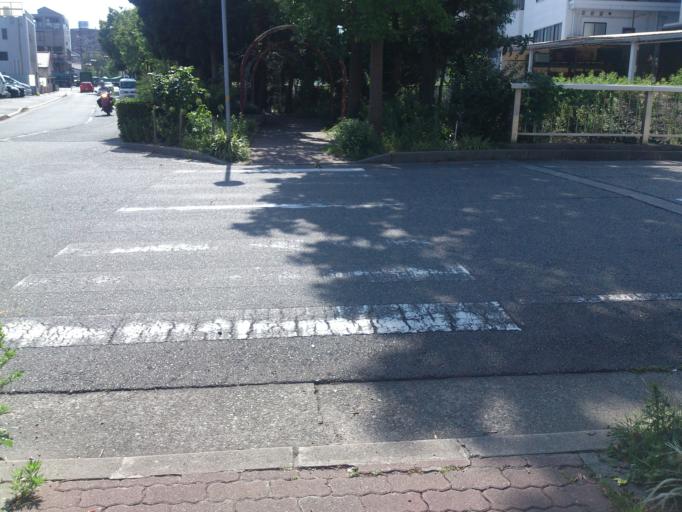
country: JP
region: Hyogo
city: Amagasaki
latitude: 34.7258
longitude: 135.4217
